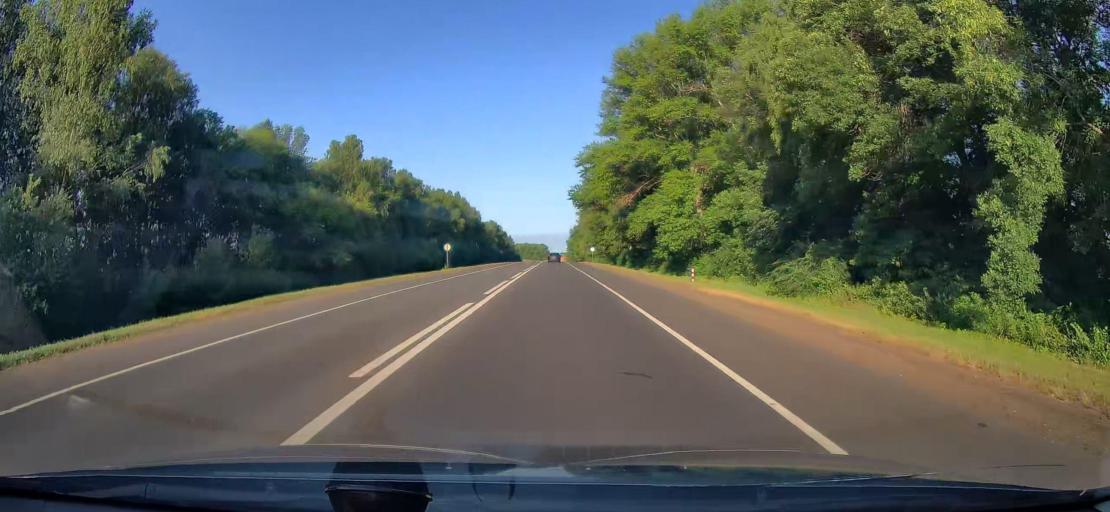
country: RU
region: Tula
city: Plavsk
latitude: 53.6811
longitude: 37.2586
